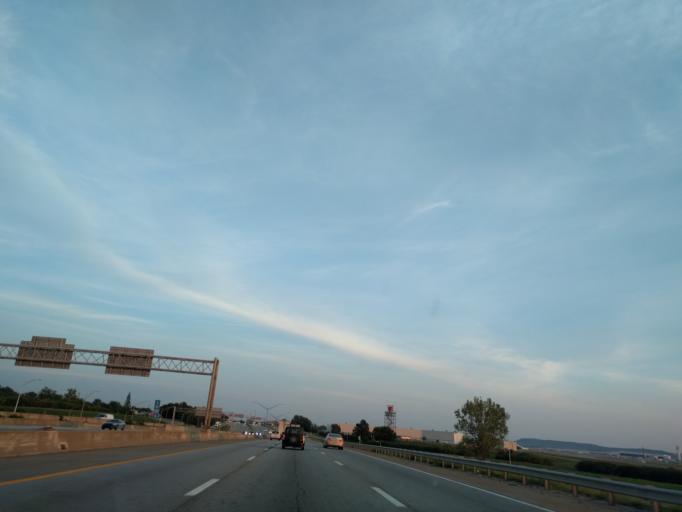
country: US
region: Kentucky
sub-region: Jefferson County
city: Audubon Park
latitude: 38.1897
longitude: -85.7289
